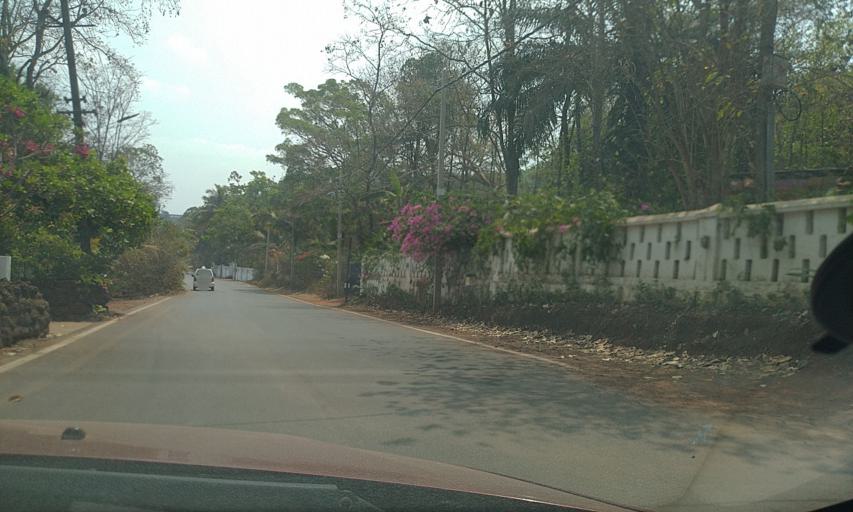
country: IN
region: Goa
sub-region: North Goa
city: Mapuca
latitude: 15.5972
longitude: 73.7883
